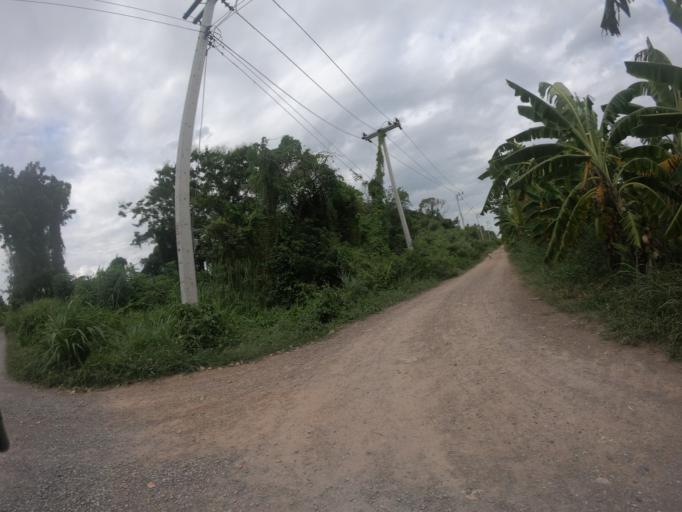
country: TH
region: Pathum Thani
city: Nong Suea
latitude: 14.0761
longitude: 100.8353
